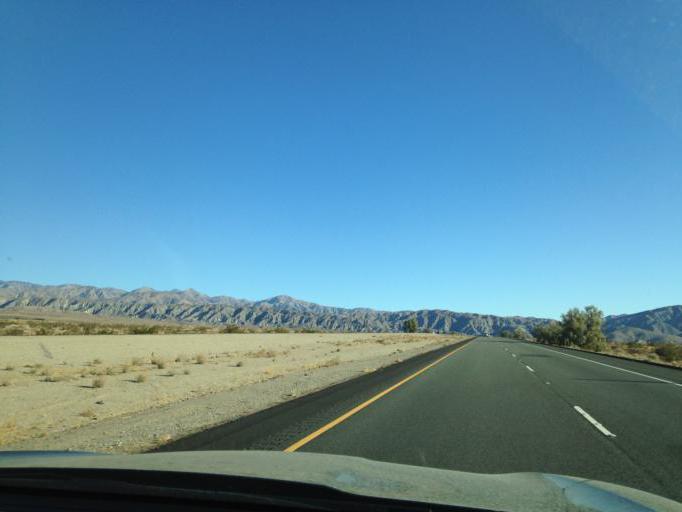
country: US
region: California
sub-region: Riverside County
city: Garnet
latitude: 33.9626
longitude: -116.5901
